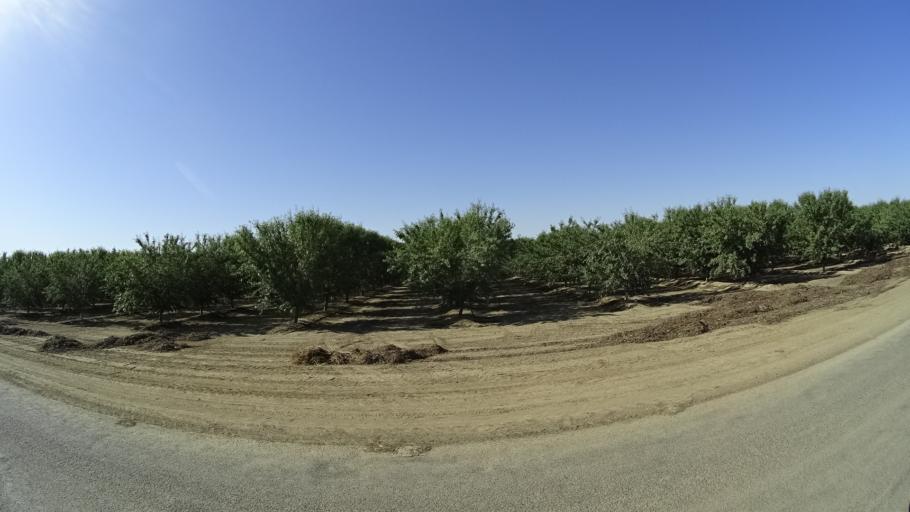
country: US
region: California
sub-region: Kings County
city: Kettleman City
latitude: 36.1088
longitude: -120.0251
